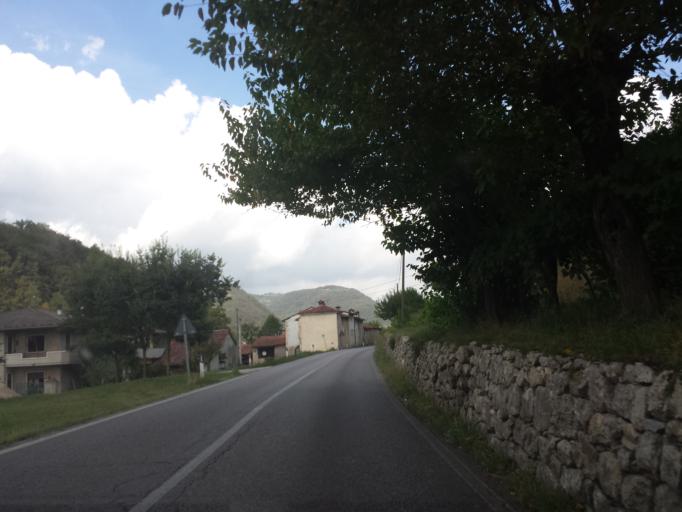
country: IT
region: Veneto
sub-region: Provincia di Vicenza
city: Gambugliano
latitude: 45.5785
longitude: 11.4177
